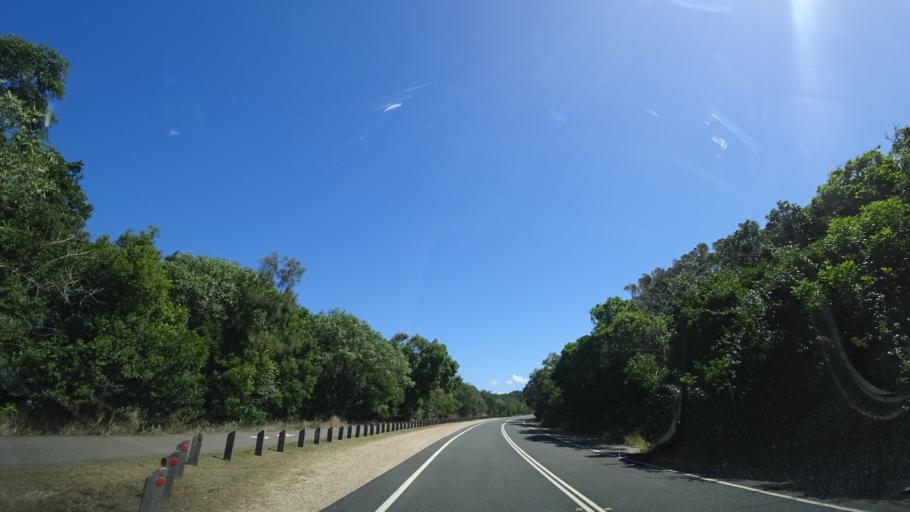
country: AU
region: Queensland
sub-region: Sunshine Coast
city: Mooloolaba
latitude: -26.6267
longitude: 153.1003
